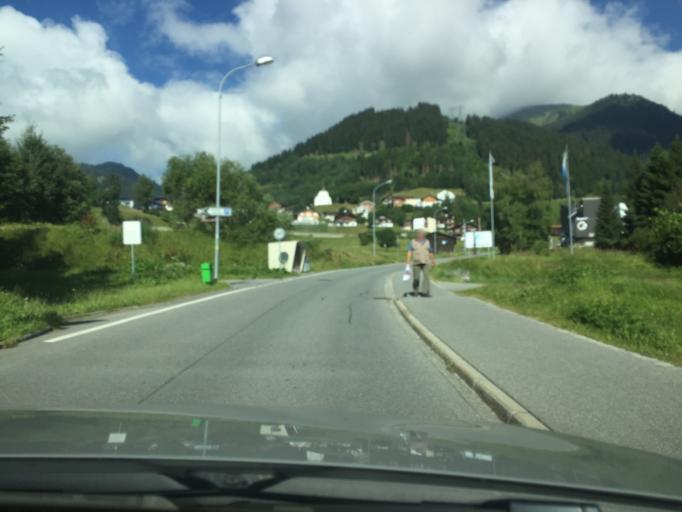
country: CH
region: Grisons
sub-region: Surselva District
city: Disentis
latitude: 46.7000
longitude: 8.8436
